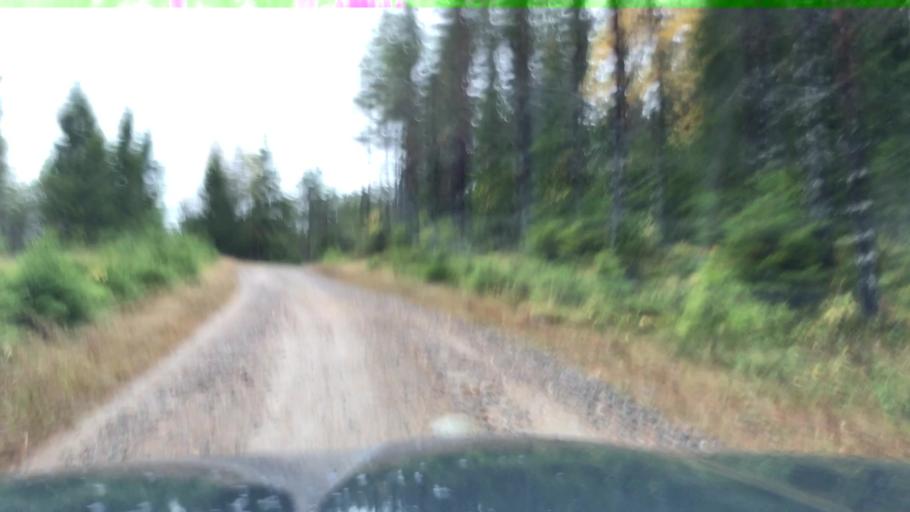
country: NO
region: Hedmark
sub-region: Trysil
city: Innbygda
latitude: 60.9266
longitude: 12.6423
